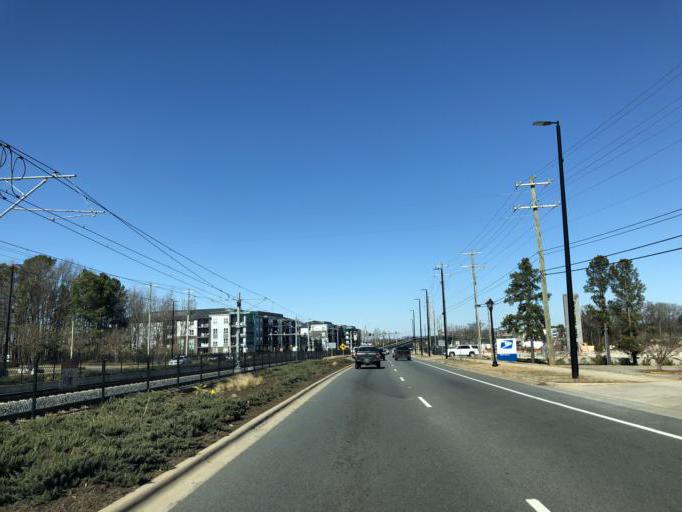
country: US
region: North Carolina
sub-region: Mecklenburg County
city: Charlotte
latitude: 35.2794
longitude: -80.7659
